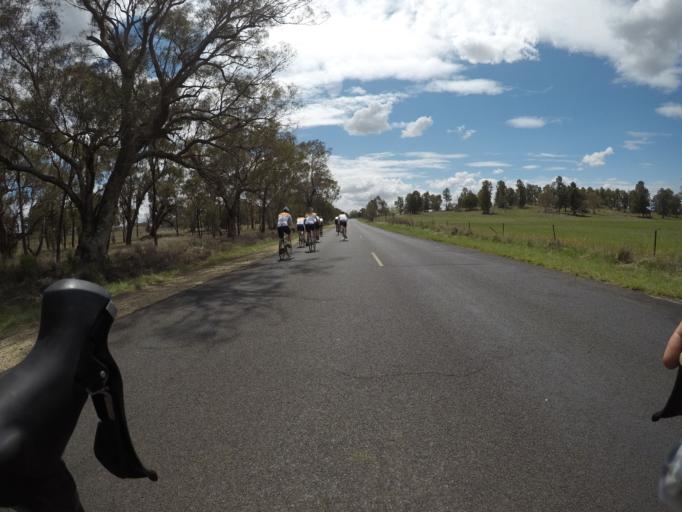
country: AU
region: New South Wales
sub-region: Dubbo Municipality
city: Dubbo
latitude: -32.2907
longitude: 148.5984
